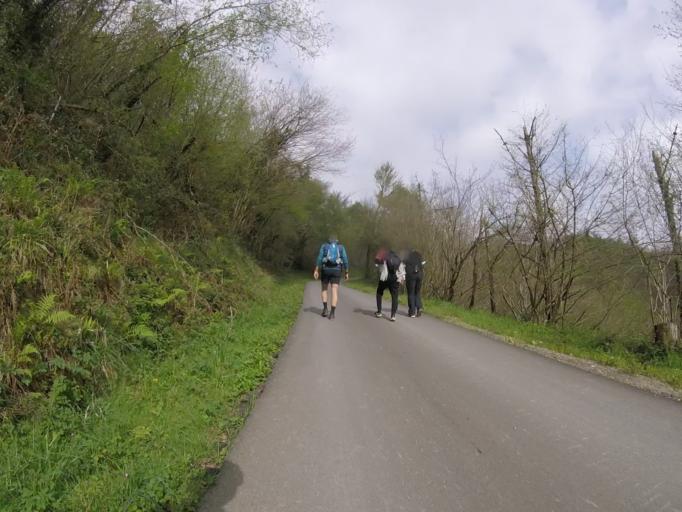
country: ES
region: Basque Country
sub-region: Provincia de Guipuzcoa
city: Asteasu
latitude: 43.2251
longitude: -2.0946
